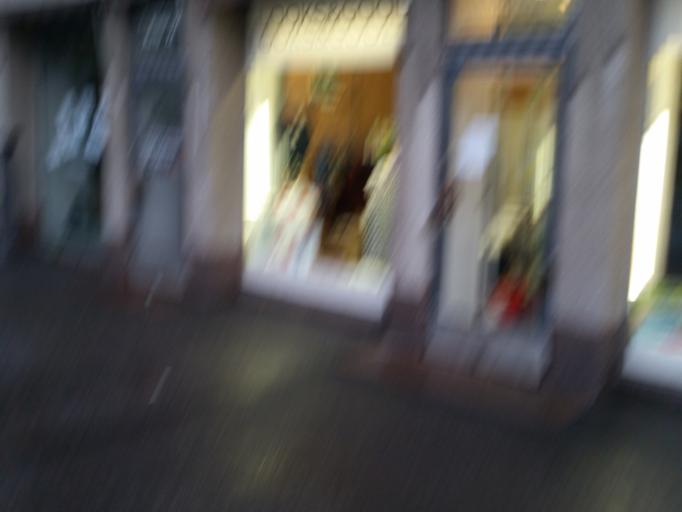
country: FI
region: Uusimaa
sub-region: Helsinki
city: Helsinki
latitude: 60.1836
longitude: 24.9183
